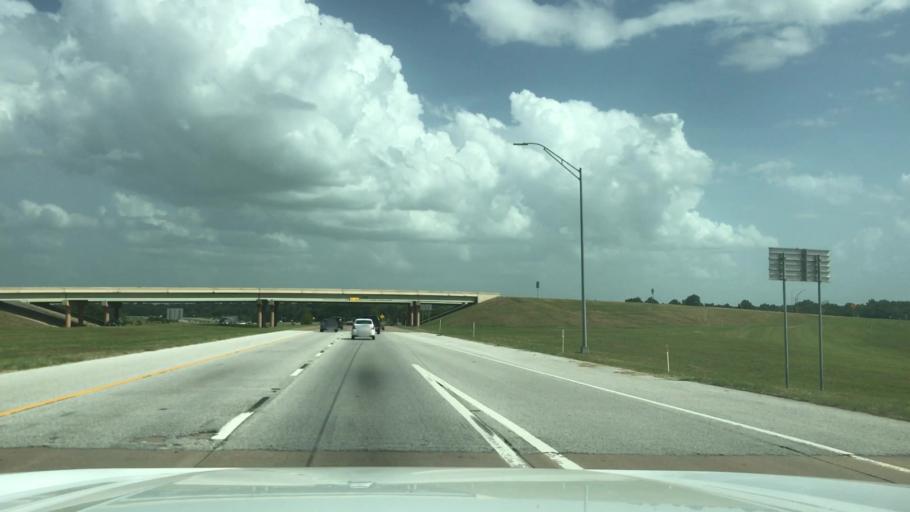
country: US
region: Texas
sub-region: Waller County
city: Hempstead
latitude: 30.1005
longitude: -96.0430
